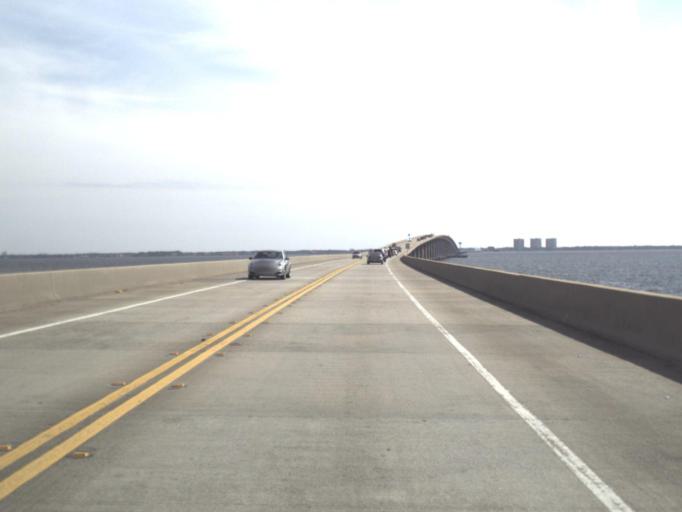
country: US
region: Florida
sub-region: Walton County
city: Miramar Beach
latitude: 30.4425
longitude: -86.4162
